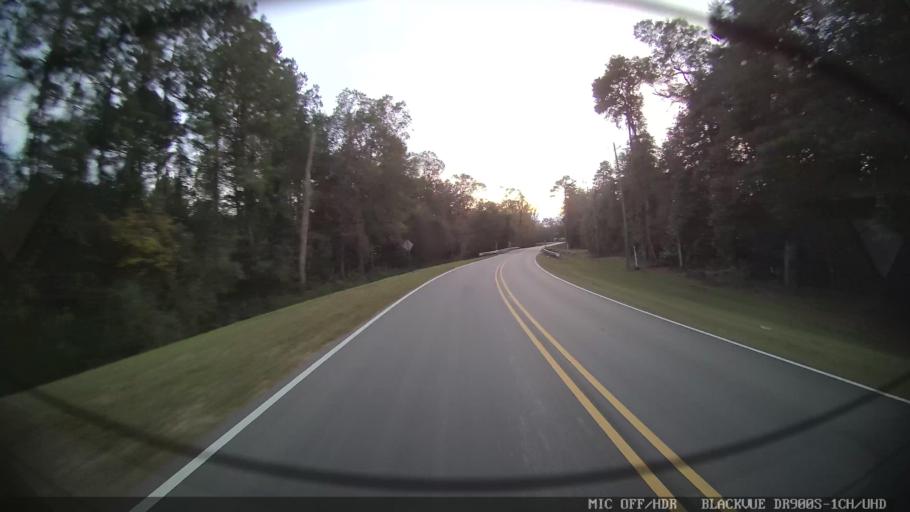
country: US
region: Mississippi
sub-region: Stone County
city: Wiggins
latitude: 31.0522
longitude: -89.1921
